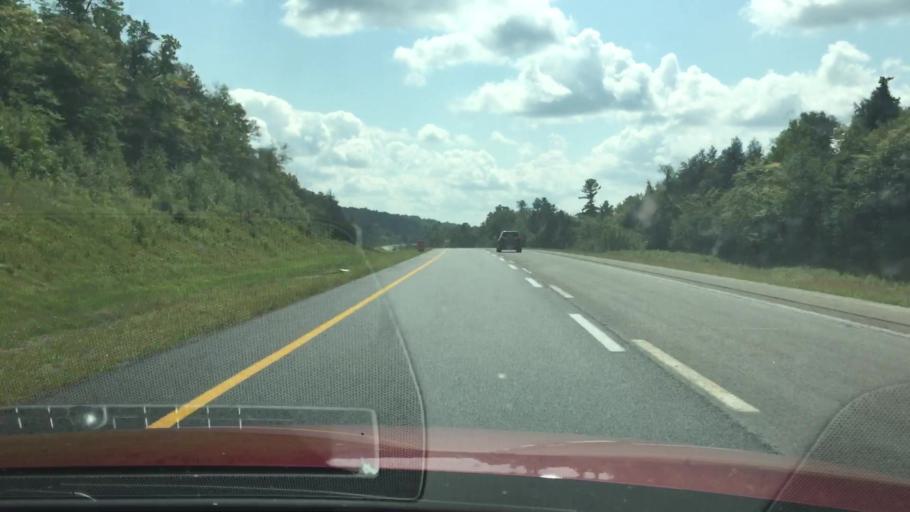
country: US
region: Maine
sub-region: Penobscot County
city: Medway
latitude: 45.7212
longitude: -68.4750
